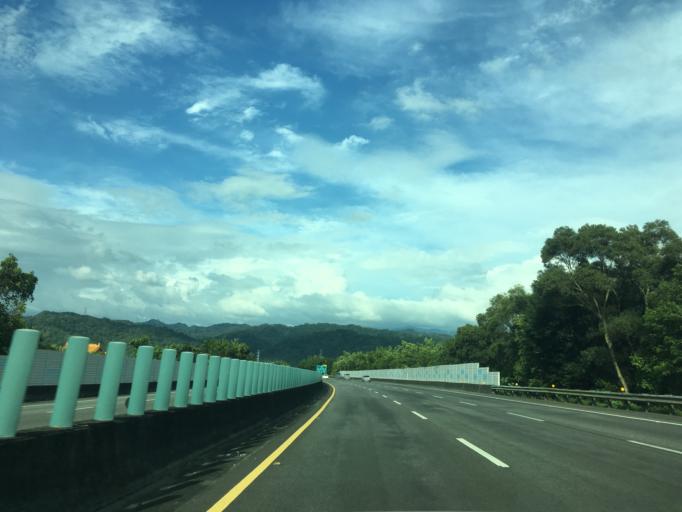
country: TW
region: Taiwan
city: Lugu
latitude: 23.7771
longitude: 120.6928
